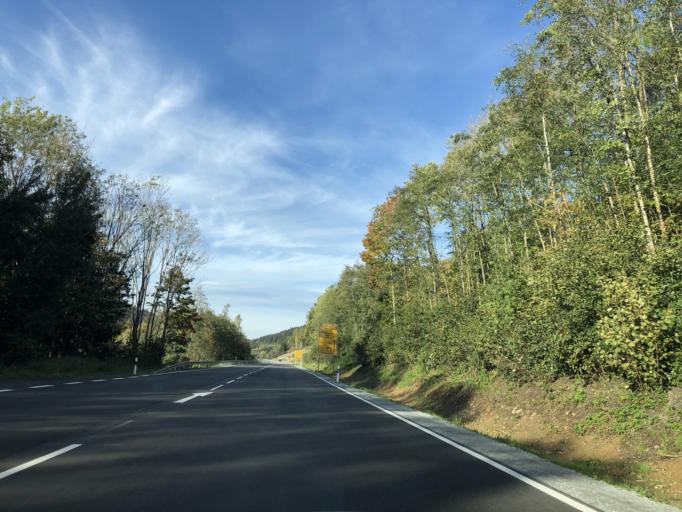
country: DE
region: Bavaria
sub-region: Lower Bavaria
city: Grafling
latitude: 48.9195
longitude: 12.9807
